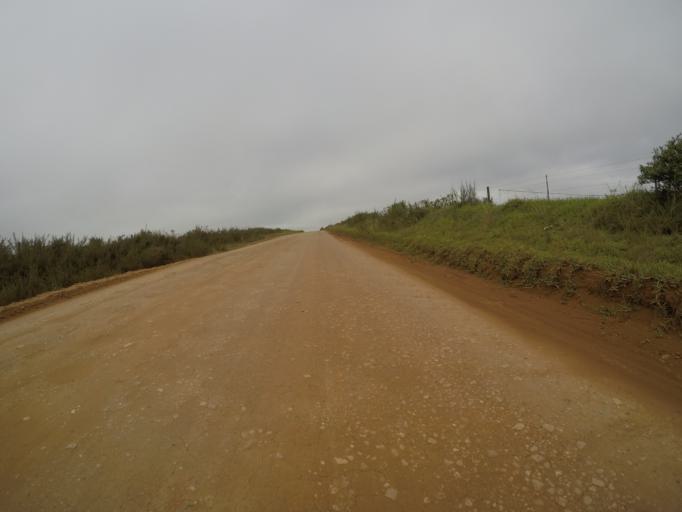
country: ZA
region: Eastern Cape
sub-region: Cacadu District Municipality
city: Kareedouw
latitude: -34.0297
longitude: 24.2436
